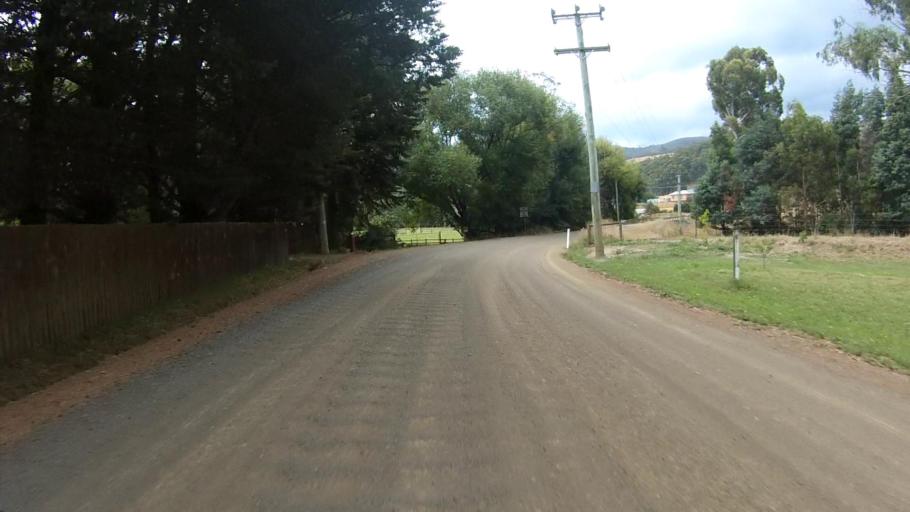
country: AU
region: Tasmania
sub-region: Huon Valley
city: Huonville
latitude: -42.9806
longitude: 147.0544
